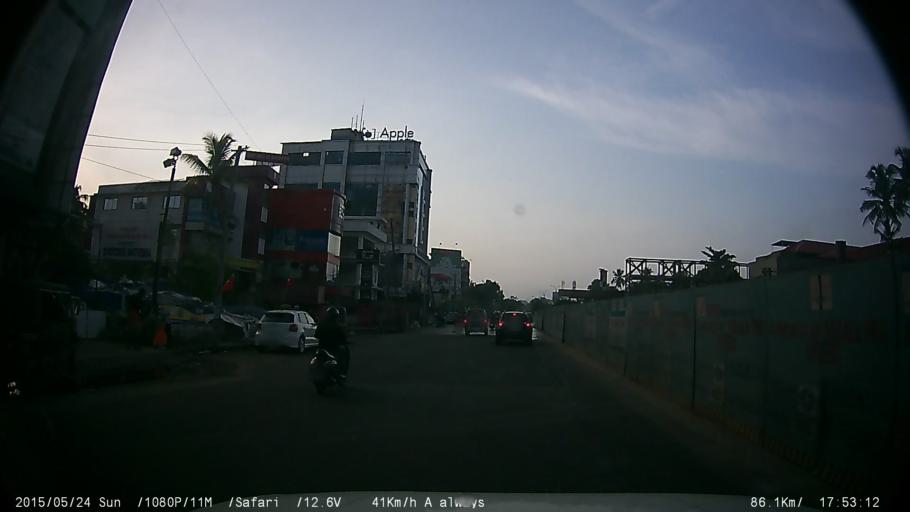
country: IN
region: Kerala
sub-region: Ernakulam
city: Elur
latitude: 10.0061
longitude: 76.3127
